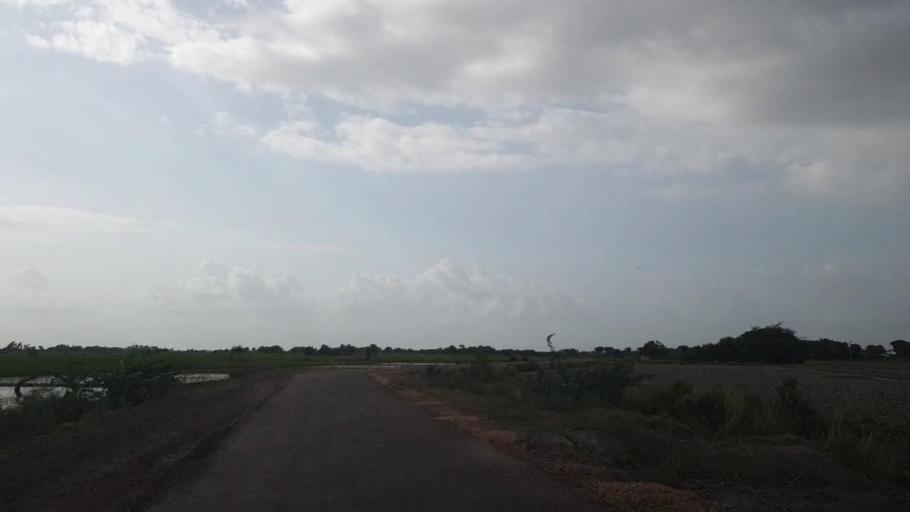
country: PK
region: Sindh
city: Kadhan
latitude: 24.5985
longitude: 69.0568
